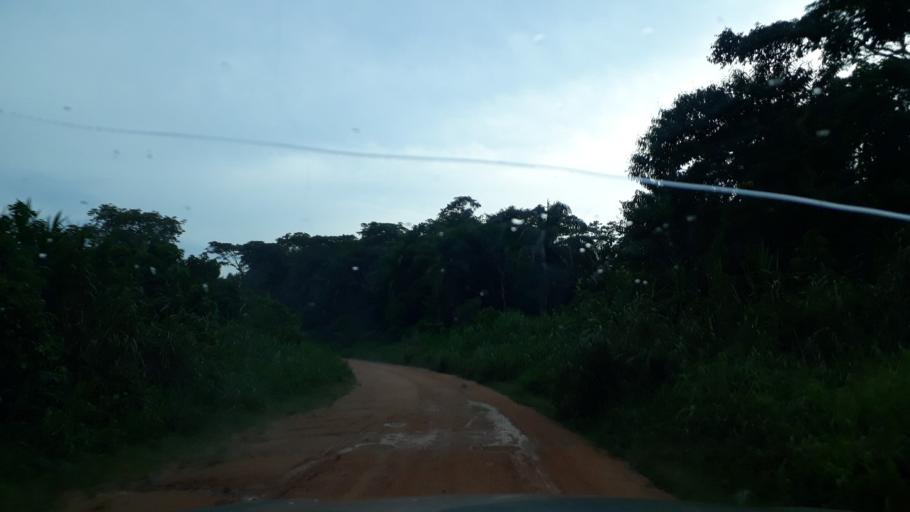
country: CD
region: Eastern Province
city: Bunia
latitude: 1.3968
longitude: 29.3722
